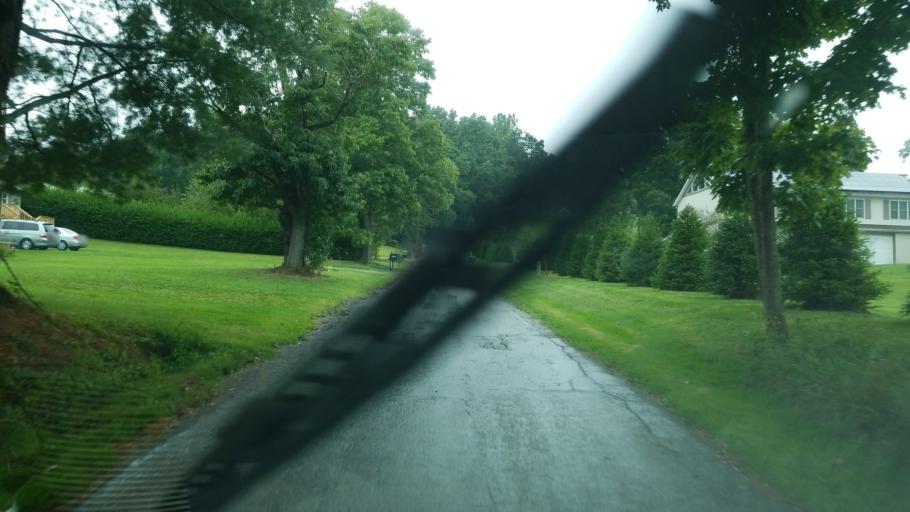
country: US
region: Ohio
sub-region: Sandusky County
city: Bellville
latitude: 40.6340
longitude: -82.4911
